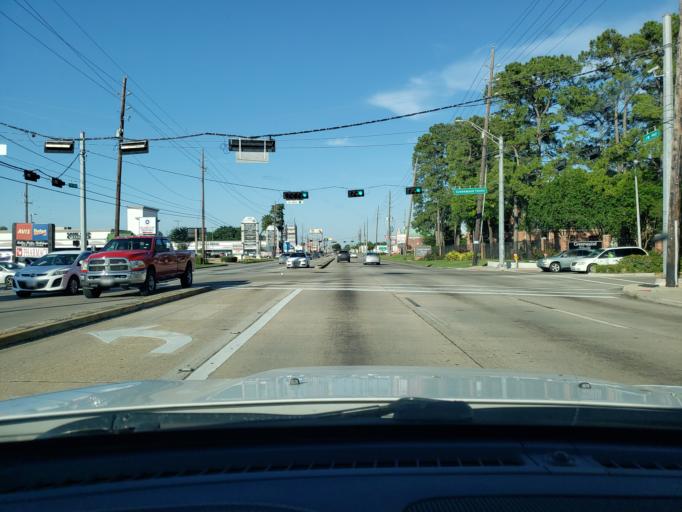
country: US
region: Texas
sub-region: Harris County
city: Hudson
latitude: 29.9830
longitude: -95.5071
